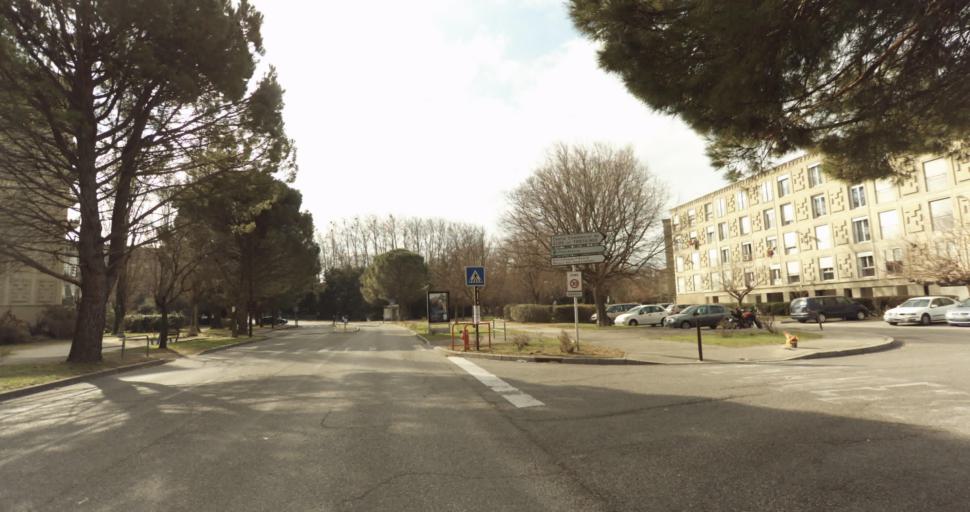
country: FR
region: Provence-Alpes-Cote d'Azur
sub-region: Departement du Vaucluse
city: Avignon
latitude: 43.9475
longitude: 4.8354
